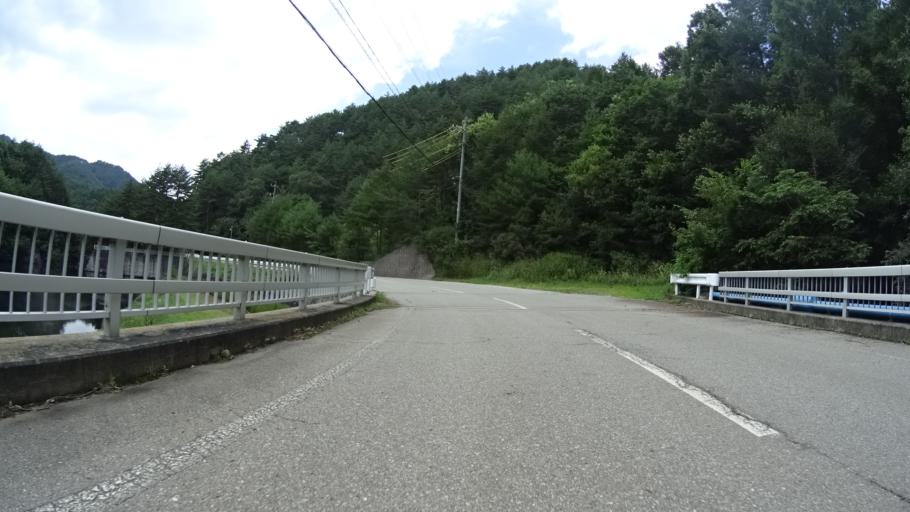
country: JP
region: Nagano
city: Saku
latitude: 36.0720
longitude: 138.6137
